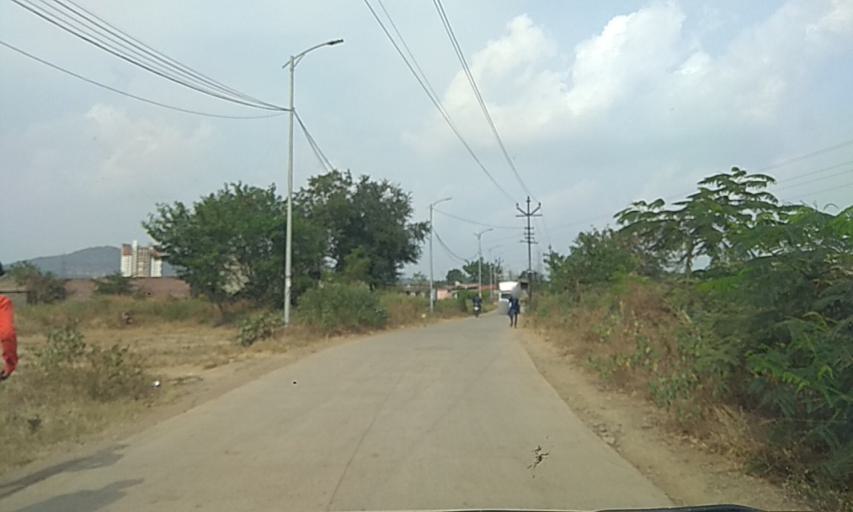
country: IN
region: Maharashtra
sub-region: Pune Division
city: Pimpri
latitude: 18.5839
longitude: 73.7058
